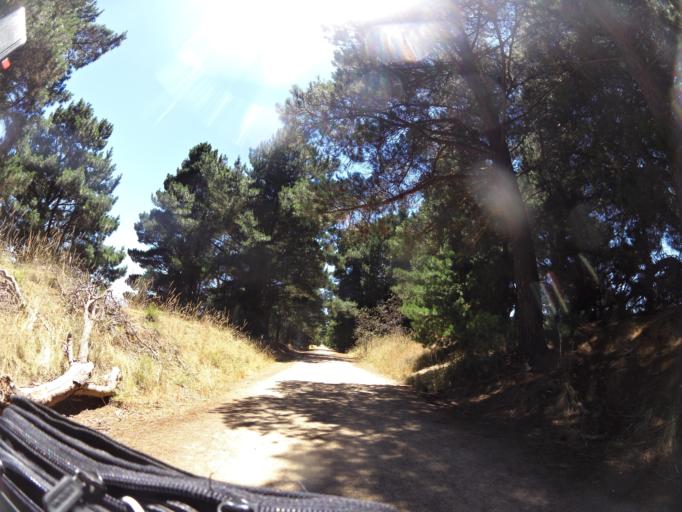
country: AU
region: Victoria
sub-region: Ballarat North
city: Delacombe
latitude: -37.5838
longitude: 143.7247
